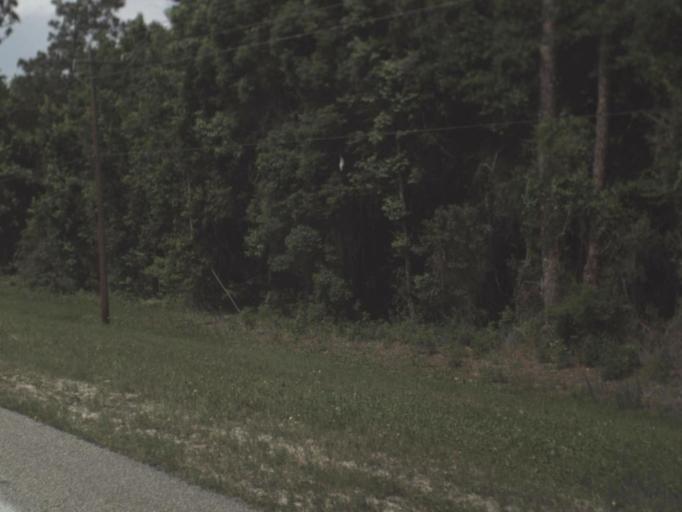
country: US
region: Florida
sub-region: Clay County
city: Green Cove Springs
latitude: 29.9224
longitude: -81.6834
